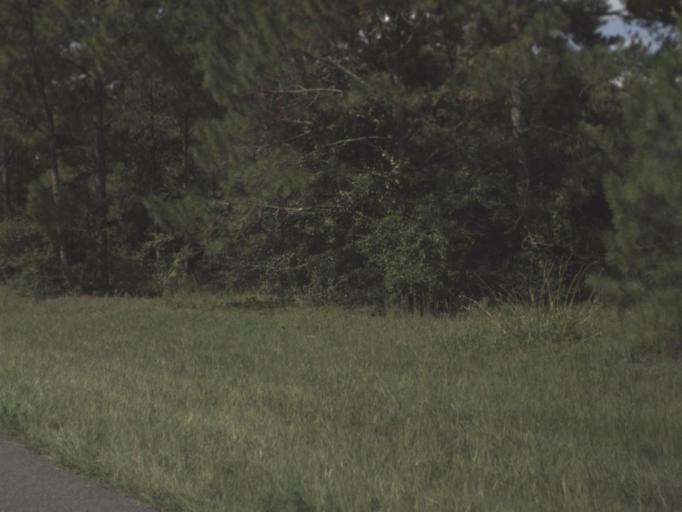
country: US
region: Florida
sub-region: Marion County
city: Dunnellon
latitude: 29.0230
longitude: -82.4562
